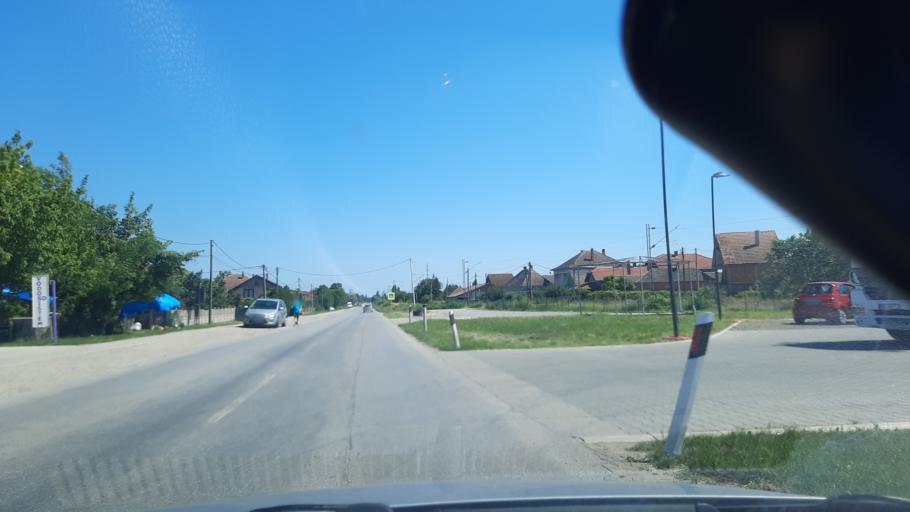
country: RS
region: Central Serbia
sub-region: Podunavski Okrug
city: Smederevo
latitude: 44.5962
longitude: 20.9912
